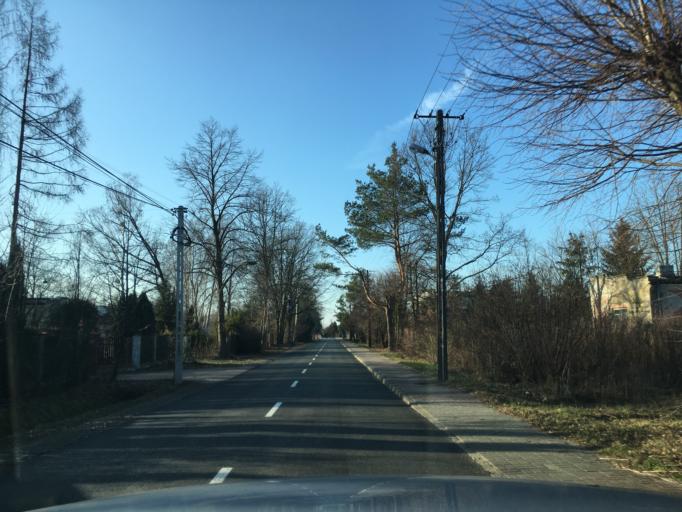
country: PL
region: Lodz Voivodeship
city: Zabia Wola
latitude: 52.0522
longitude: 20.7318
